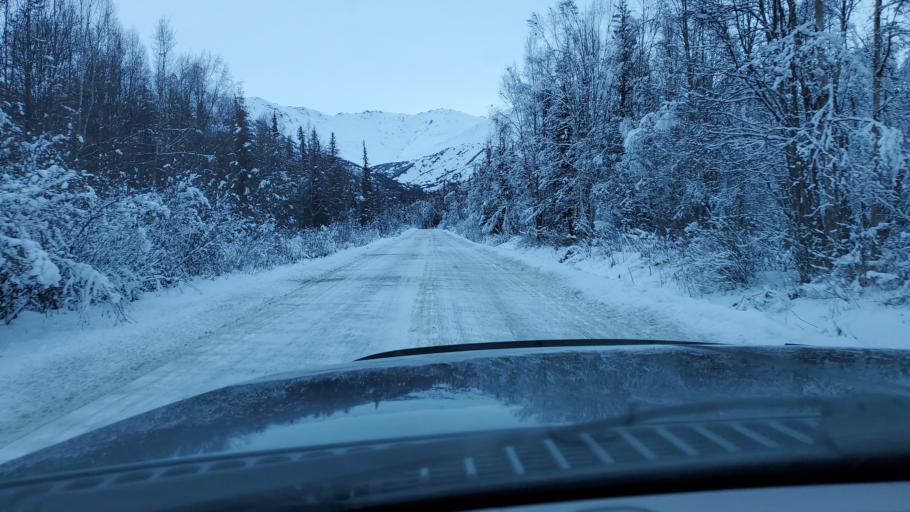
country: US
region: Alaska
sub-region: Matanuska-Susitna Borough
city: Lakes
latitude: 61.6937
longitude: -149.3225
